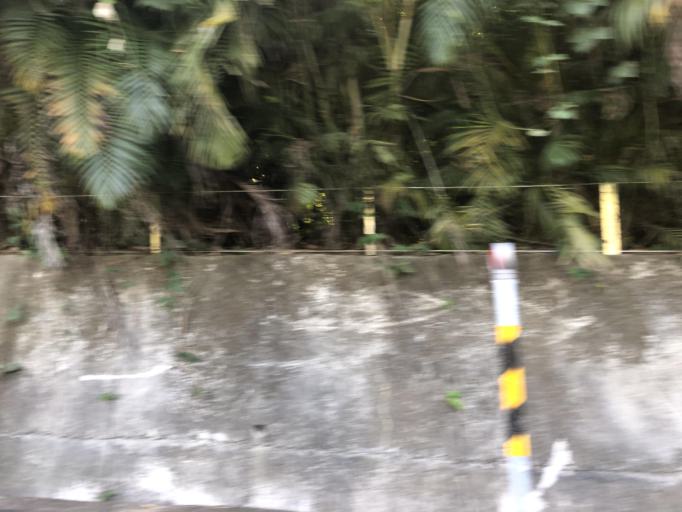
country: TW
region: Taiwan
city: Yujing
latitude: 23.0091
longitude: 120.3871
